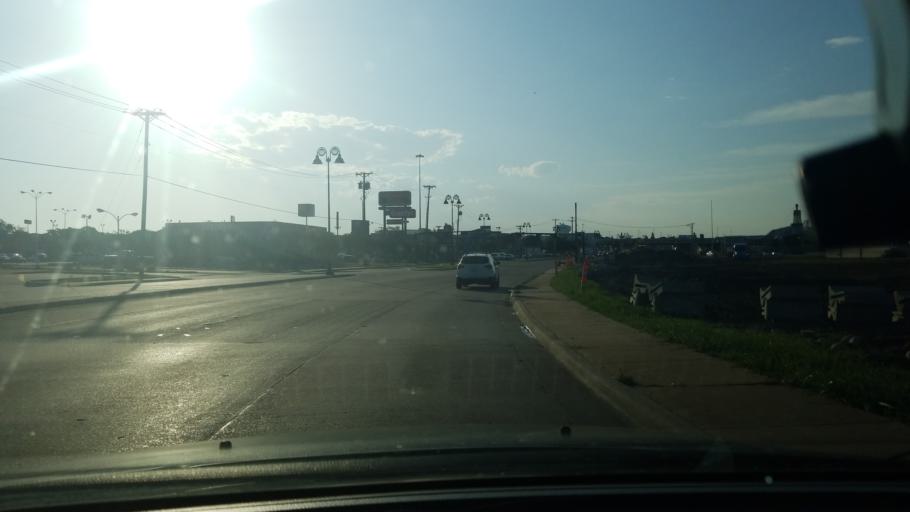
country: US
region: Texas
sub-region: Dallas County
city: Mesquite
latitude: 32.8115
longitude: -96.6320
